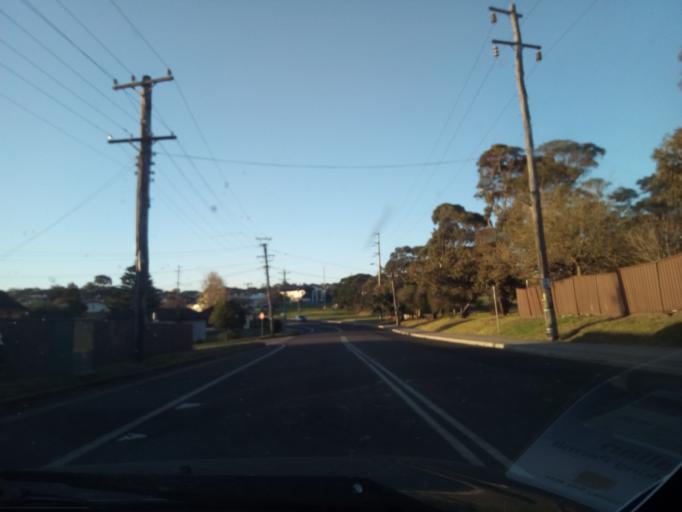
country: AU
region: New South Wales
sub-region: Wollongong
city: Port Kembla
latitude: -34.4912
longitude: 150.8940
